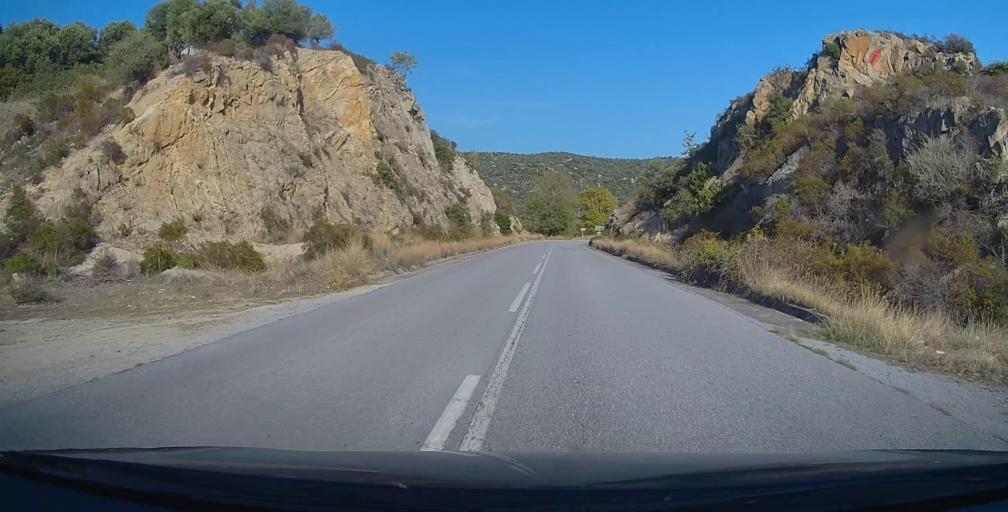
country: GR
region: Central Macedonia
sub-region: Nomos Chalkidikis
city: Sykia
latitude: 40.0059
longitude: 23.8826
